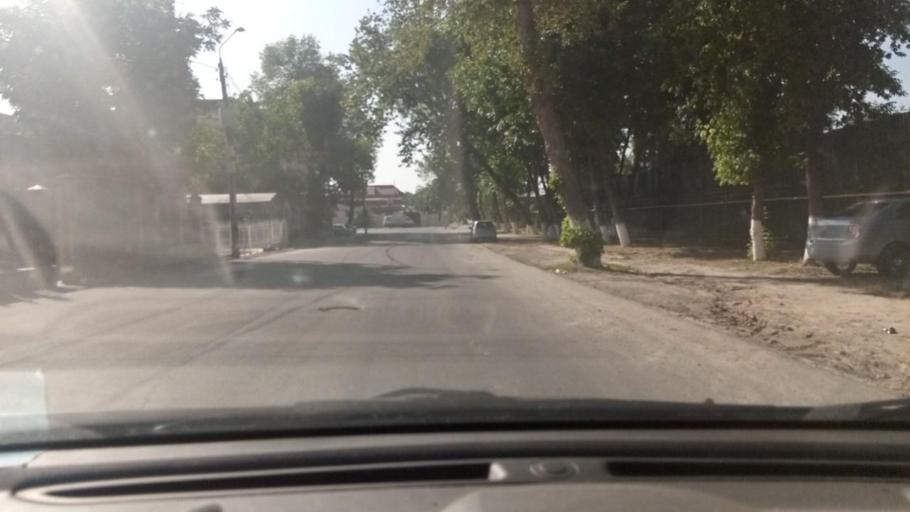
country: UZ
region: Toshkent
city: Salor
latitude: 41.3356
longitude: 69.3587
